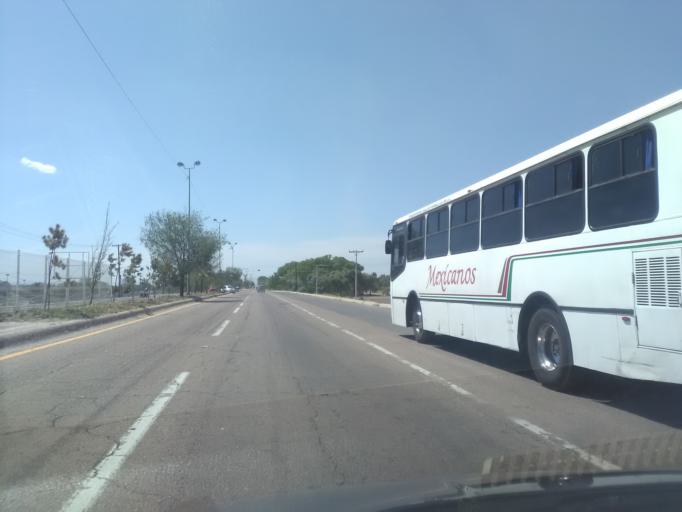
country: MX
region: Durango
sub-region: Durango
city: Jose Refugio Salcido
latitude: 24.0242
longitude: -104.5536
